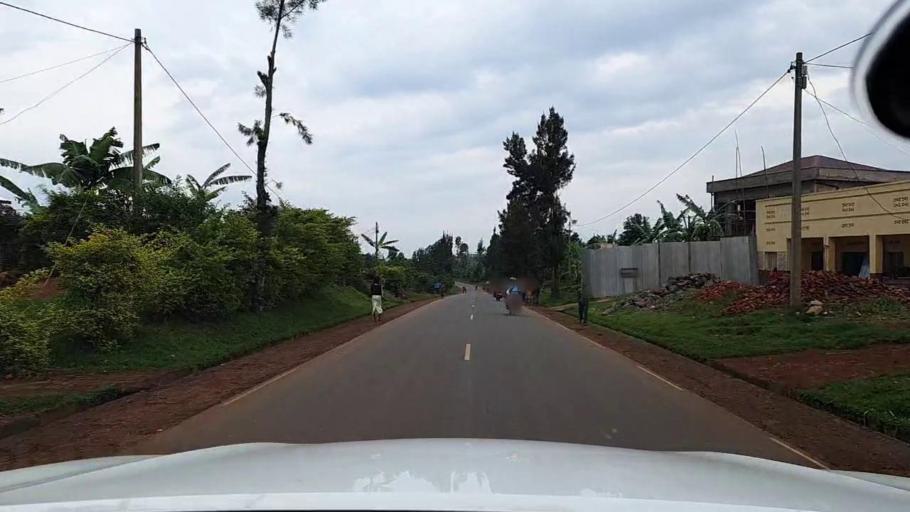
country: RW
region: Western Province
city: Cyangugu
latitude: -2.6065
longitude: 28.9343
